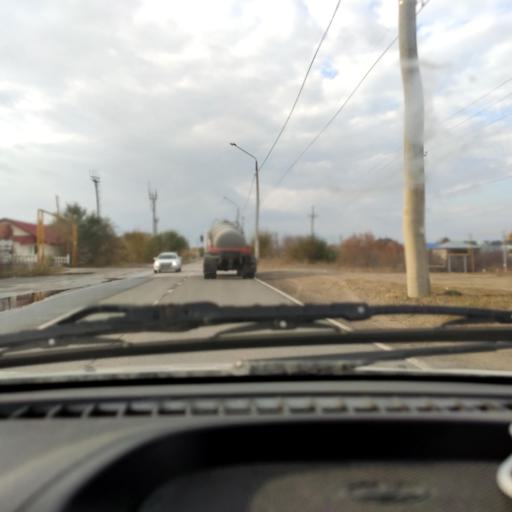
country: RU
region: Samara
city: Zhigulevsk
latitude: 53.4645
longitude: 49.5940
